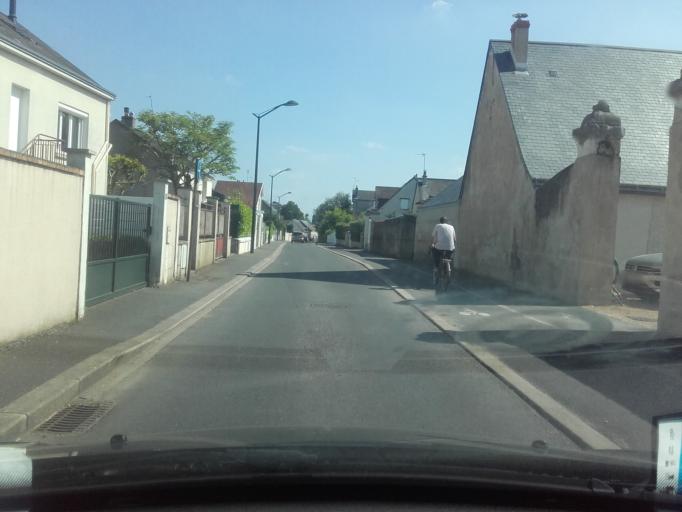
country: FR
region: Centre
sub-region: Departement d'Indre-et-Loire
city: Saint-Cyr-sur-Loire
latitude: 47.4167
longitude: 0.6751
